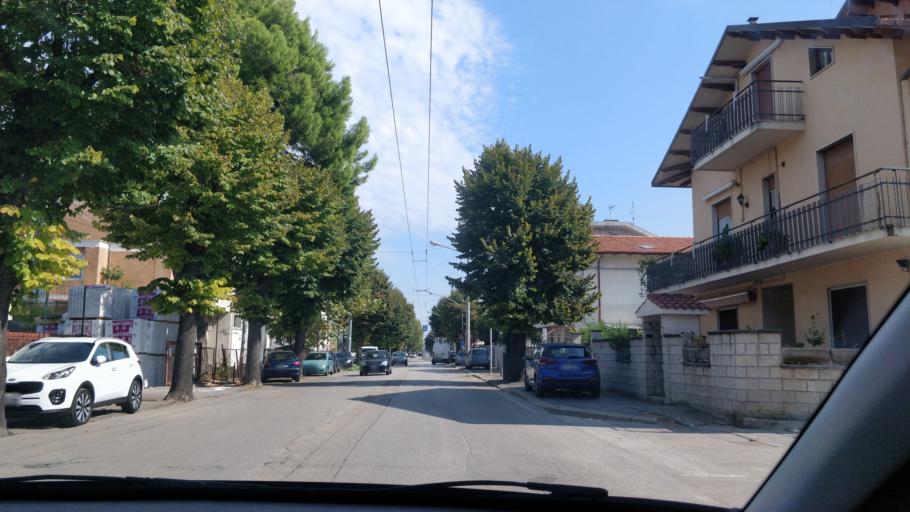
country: IT
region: Abruzzo
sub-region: Provincia di Chieti
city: Chieti
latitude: 42.3780
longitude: 14.1473
